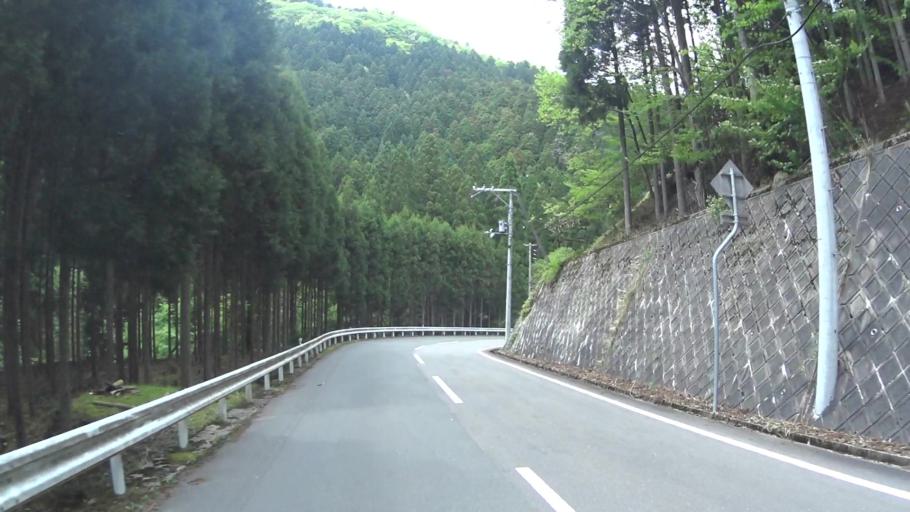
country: JP
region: Kyoto
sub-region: Kyoto-shi
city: Kamigyo-ku
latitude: 35.1827
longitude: 135.7338
